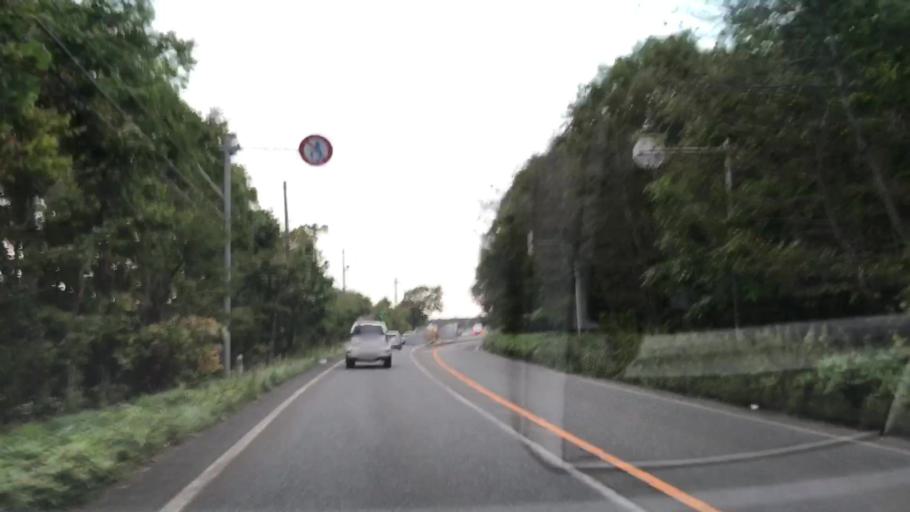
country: JP
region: Hokkaido
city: Tomakomai
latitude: 42.7063
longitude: 141.6628
